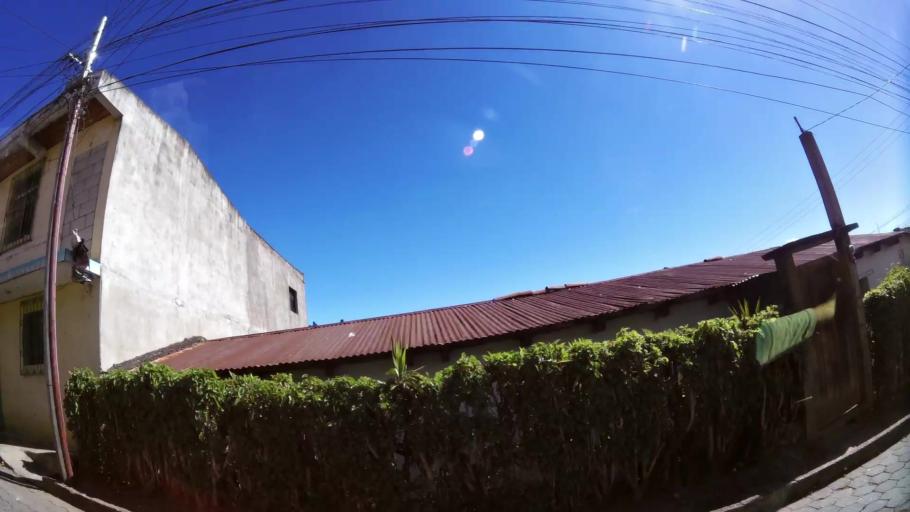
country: GT
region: Solola
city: Solola
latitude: 14.7675
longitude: -91.1814
